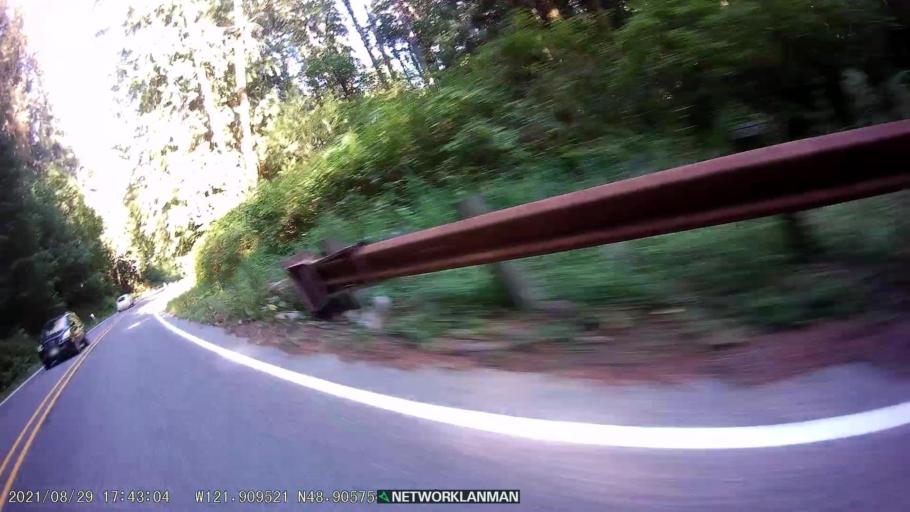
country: US
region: Washington
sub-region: Whatcom County
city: Peaceful Valley
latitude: 48.9060
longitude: -121.9092
